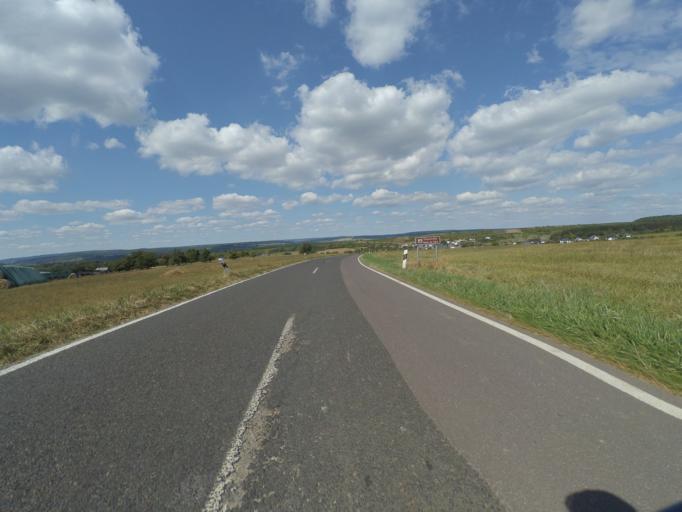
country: LU
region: Grevenmacher
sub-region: Canton de Grevenmacher
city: Wormeldange
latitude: 49.5837
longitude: 6.4193
